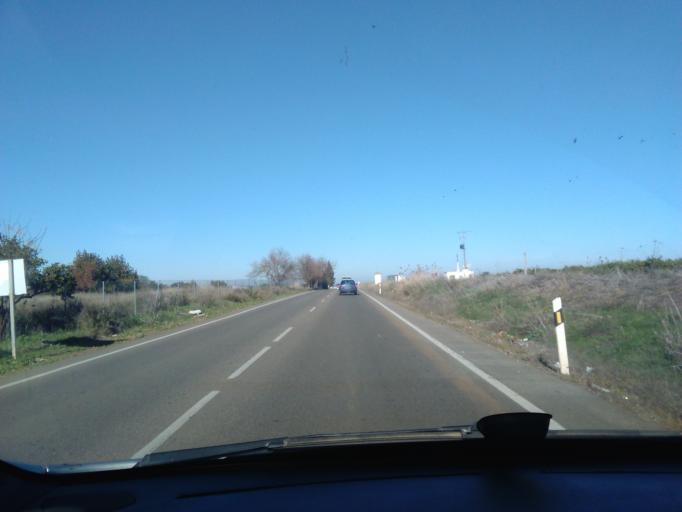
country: ES
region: Andalusia
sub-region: Provincia de Sevilla
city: La Rinconada
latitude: 37.4403
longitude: -5.9387
